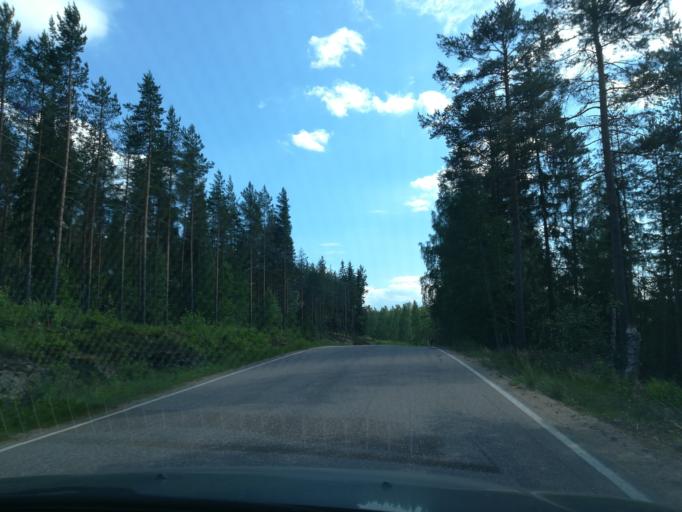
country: FI
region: South Karelia
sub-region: Imatra
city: Ruokolahti
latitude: 61.4842
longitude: 28.7860
